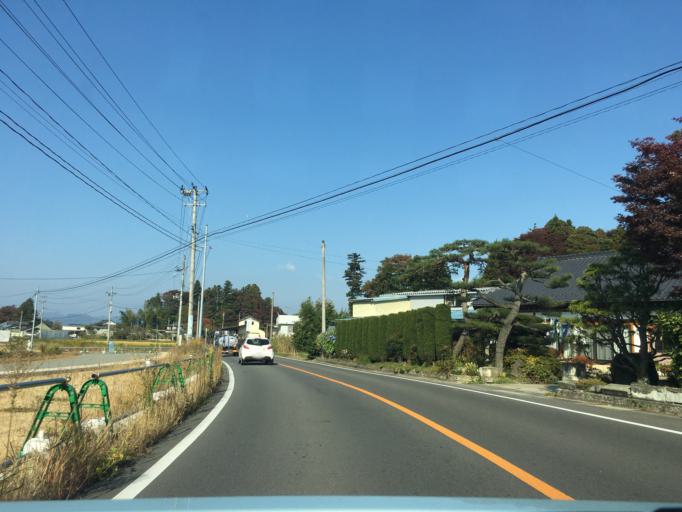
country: JP
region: Fukushima
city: Sukagawa
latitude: 37.2800
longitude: 140.3156
